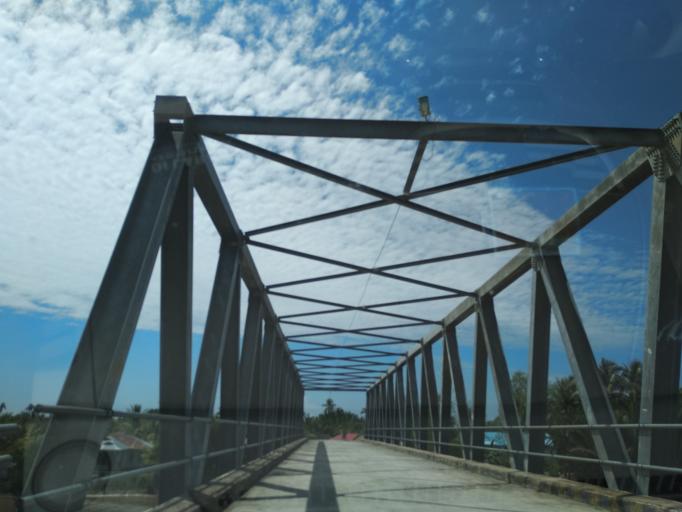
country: ID
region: South Kalimantan
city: Tabunganen
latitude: -3.4015
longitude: 114.4912
